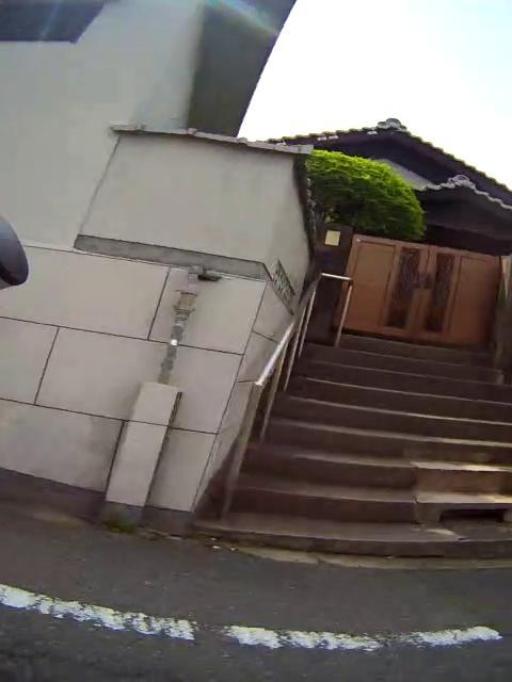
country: JP
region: Osaka
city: Toyonaka
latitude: 34.7867
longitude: 135.4822
